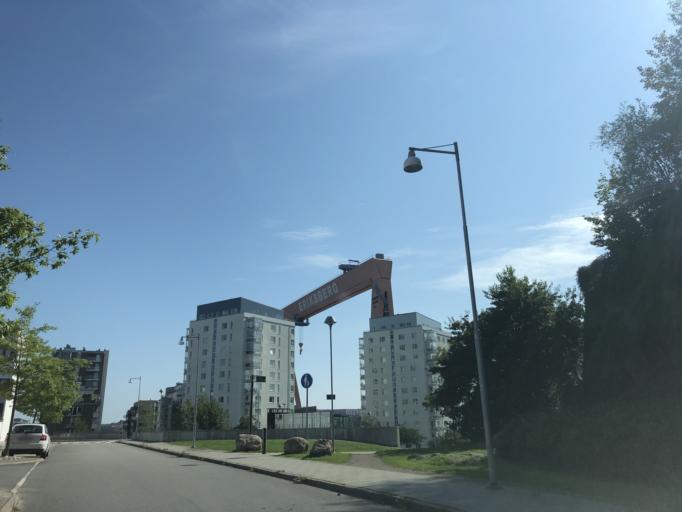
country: SE
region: Vaestra Goetaland
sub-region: Goteborg
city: Majorna
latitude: 57.6982
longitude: 11.9046
